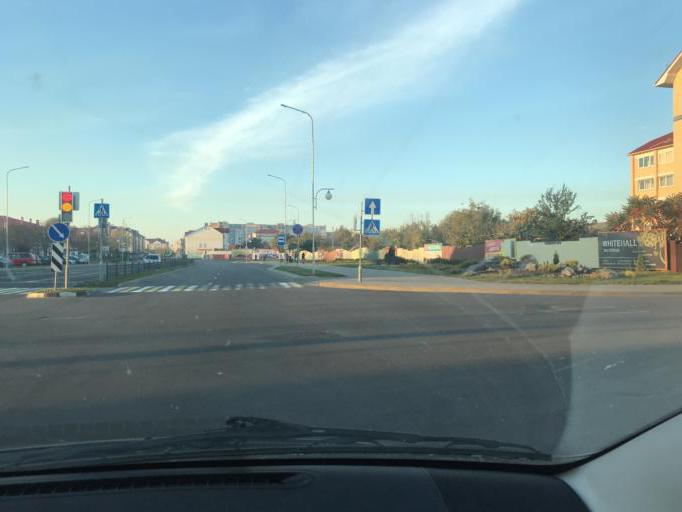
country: BY
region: Brest
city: Pinsk
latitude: 52.1152
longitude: 26.1032
